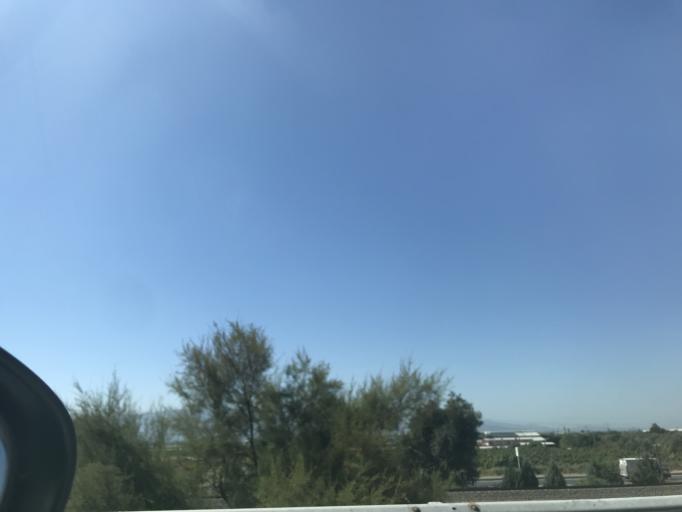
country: TR
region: Aydin
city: Germencik
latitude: 37.8702
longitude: 27.6407
